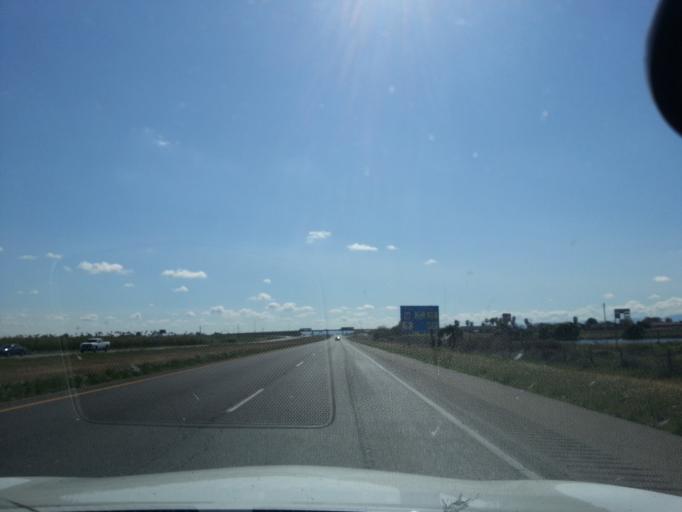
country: US
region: California
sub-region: Fresno County
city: Huron
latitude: 36.2615
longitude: -120.2487
